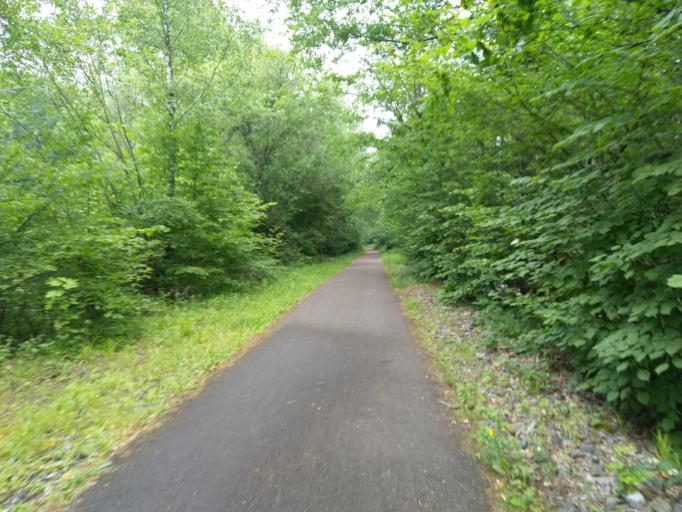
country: BE
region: Wallonia
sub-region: Province de Namur
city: Mettet
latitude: 50.3024
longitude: 4.7567
